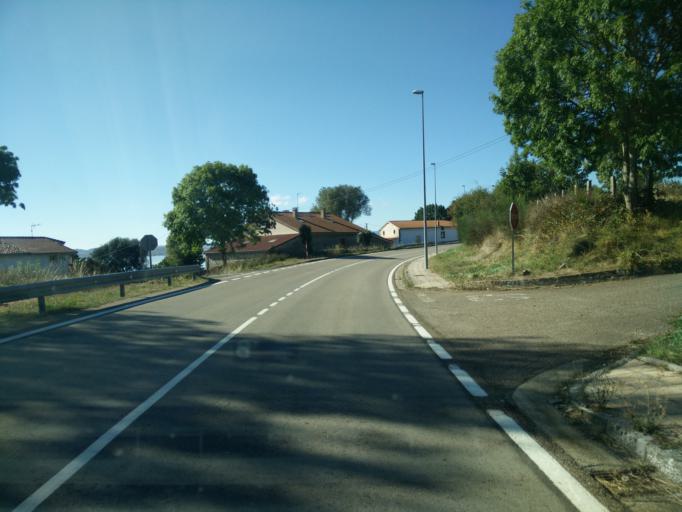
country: ES
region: Castille and Leon
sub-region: Provincia de Burgos
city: Arija
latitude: 43.0318
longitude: -3.9409
